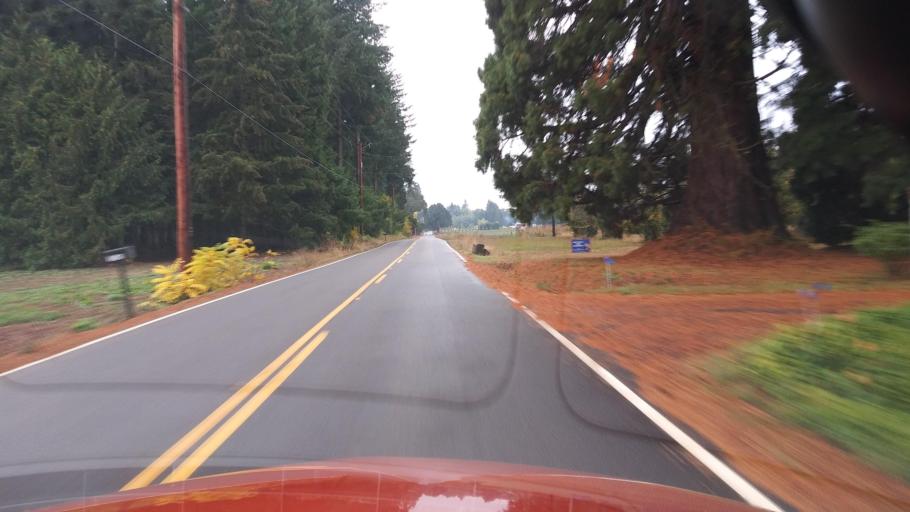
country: US
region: Oregon
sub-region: Washington County
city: Forest Grove
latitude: 45.5375
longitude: -123.0871
